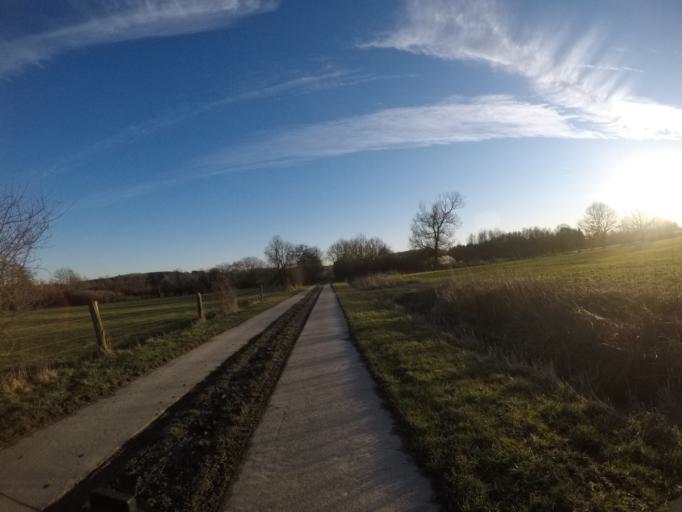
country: BE
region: Wallonia
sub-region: Province du Luxembourg
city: Habay-la-Vieille
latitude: 49.7245
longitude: 5.6011
